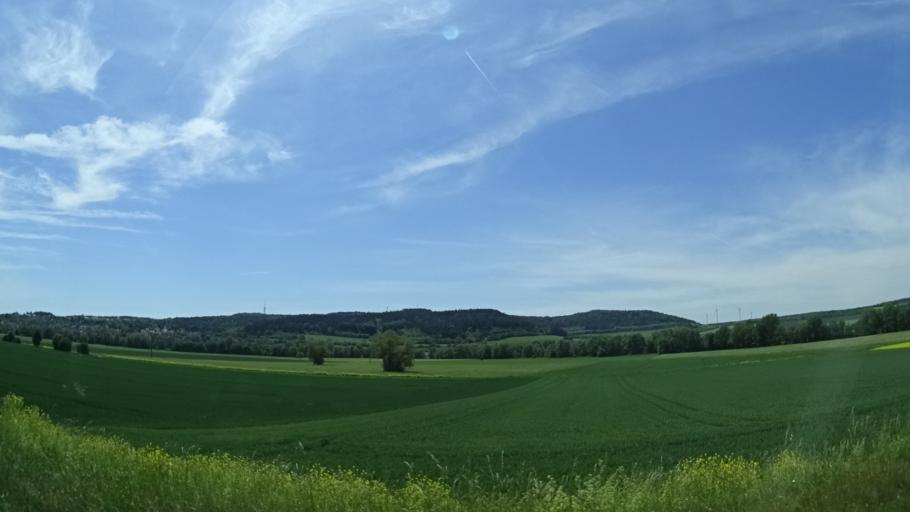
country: DE
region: Bavaria
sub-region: Regierungsbezirk Unterfranken
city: Burglauer
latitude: 50.2614
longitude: 10.1955
